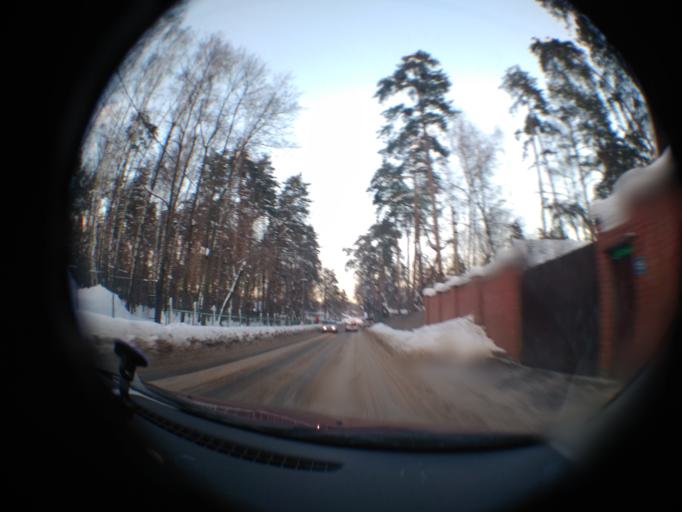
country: RU
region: Moskovskaya
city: Bykovo
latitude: 55.6162
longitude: 38.0938
